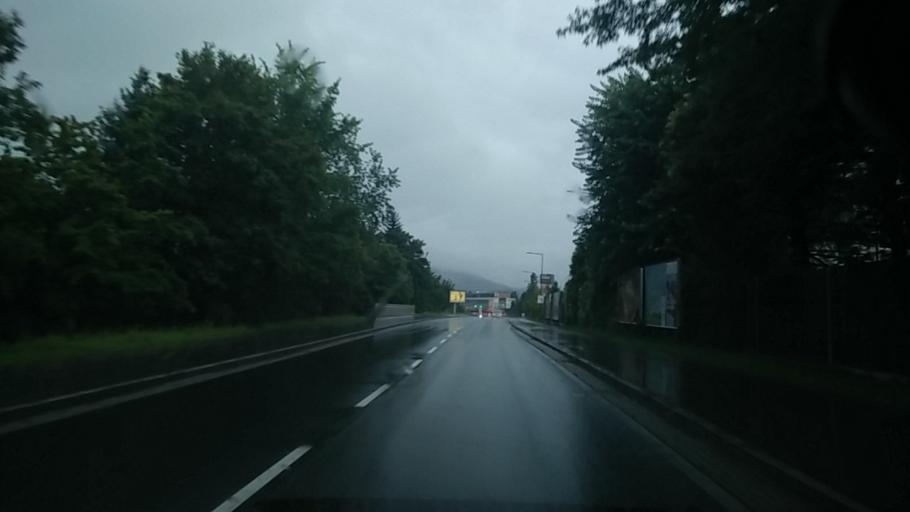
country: AT
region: Carinthia
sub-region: Villach Stadt
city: Villach
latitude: 46.6032
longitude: 13.8422
